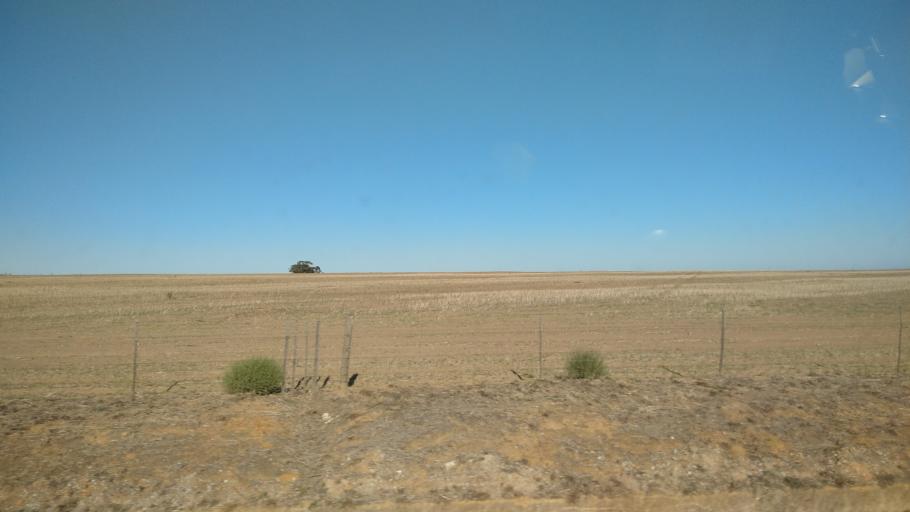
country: ZA
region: Western Cape
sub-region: West Coast District Municipality
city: Malmesbury
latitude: -33.3559
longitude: 18.6442
